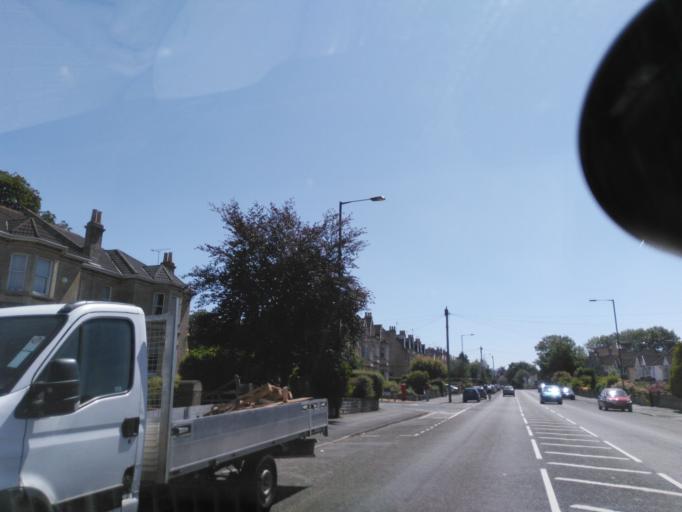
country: GB
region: England
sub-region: Bath and North East Somerset
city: Bath
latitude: 51.3863
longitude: -2.3978
